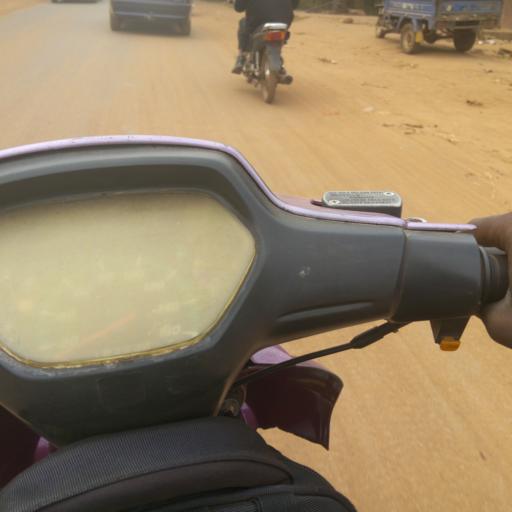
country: ML
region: Bamako
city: Bamako
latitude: 12.6643
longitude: -7.9358
